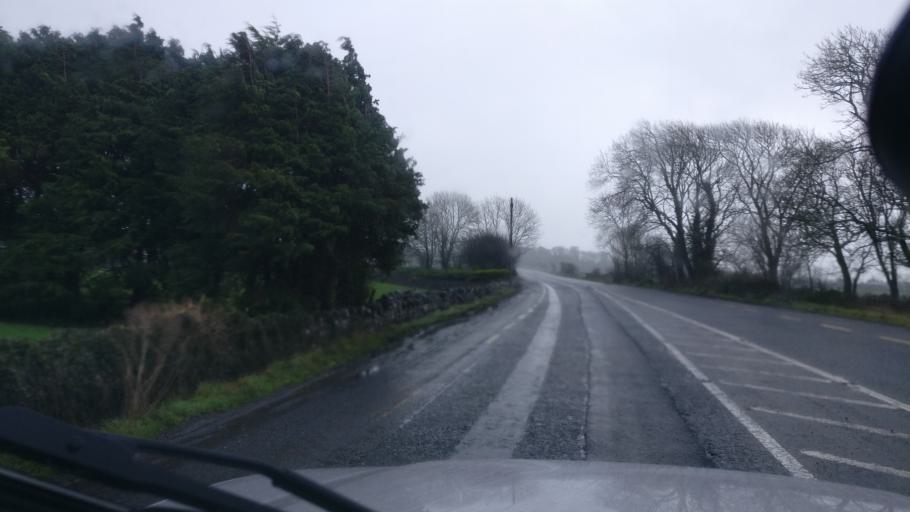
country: IE
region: Connaught
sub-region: County Galway
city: Oranmore
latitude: 53.2746
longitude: -8.8513
